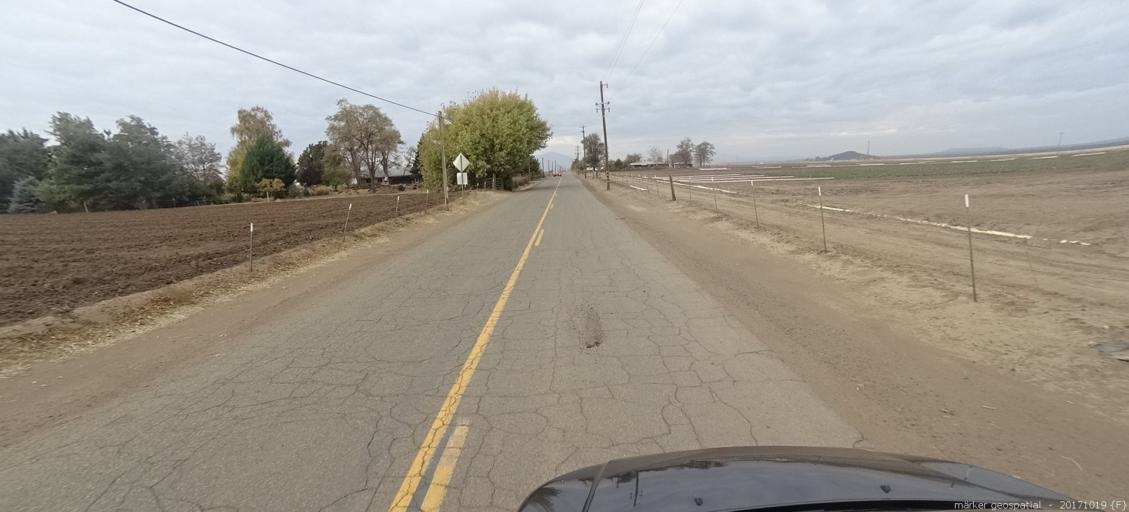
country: US
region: California
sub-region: Shasta County
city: Burney
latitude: 41.0806
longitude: -121.3330
